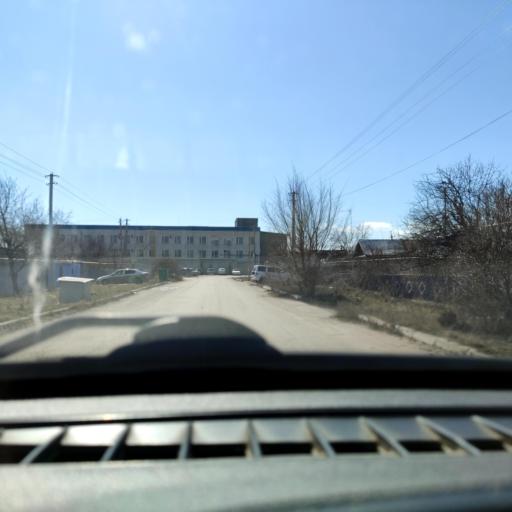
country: RU
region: Samara
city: Tol'yatti
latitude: 53.5749
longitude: 49.3049
